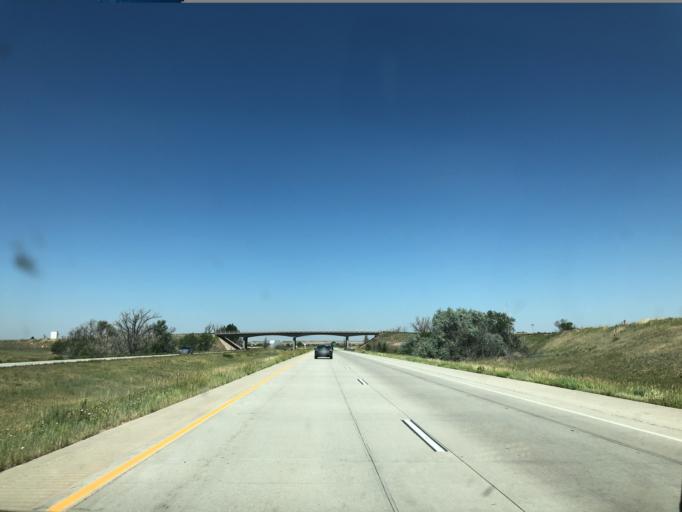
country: US
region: Colorado
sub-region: Arapahoe County
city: Byers
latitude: 39.7098
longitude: -104.2056
